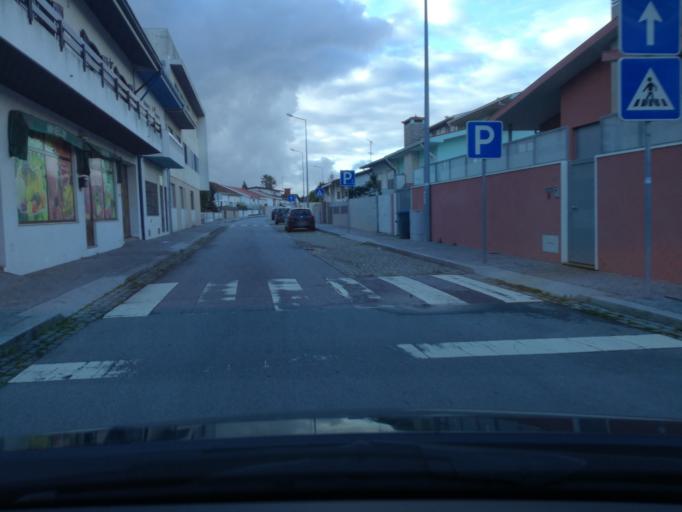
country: PT
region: Porto
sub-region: Maia
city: Gemunde
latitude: 41.2526
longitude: -8.6618
